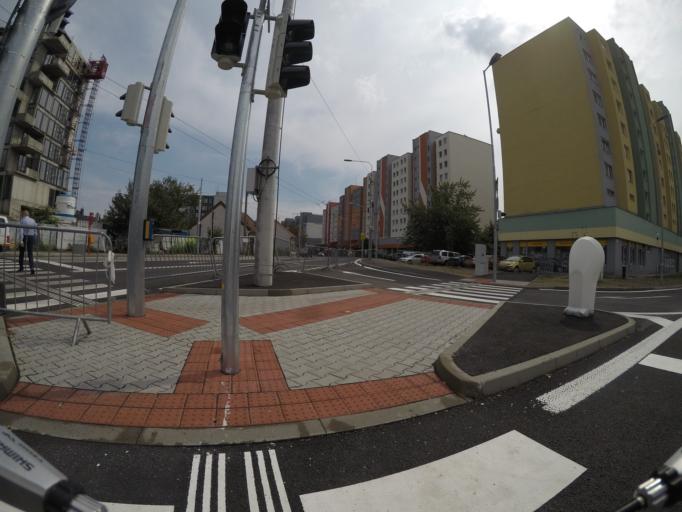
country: SK
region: Bratislavsky
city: Bratislava
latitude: 48.1490
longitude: 17.1580
